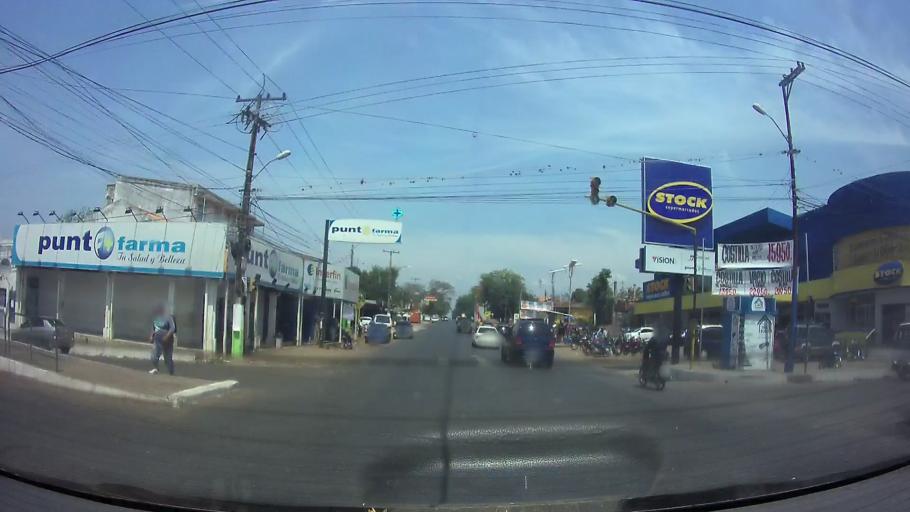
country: PY
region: Central
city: Guarambare
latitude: -25.4412
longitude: -57.4426
